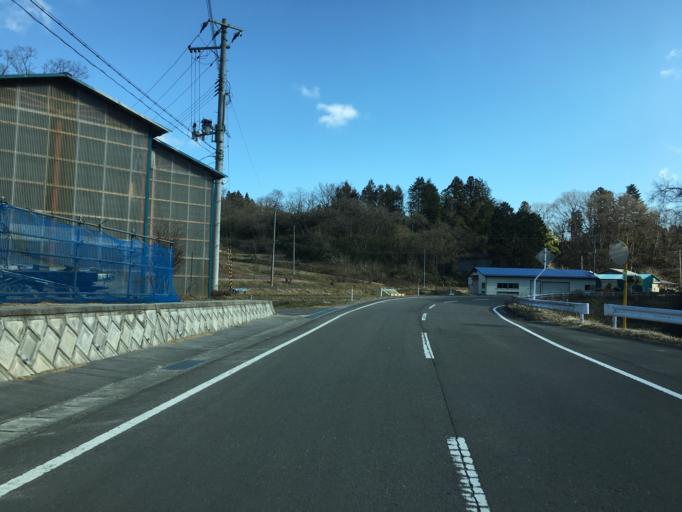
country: JP
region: Fukushima
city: Funehikimachi-funehiki
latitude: 37.4194
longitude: 140.5550
